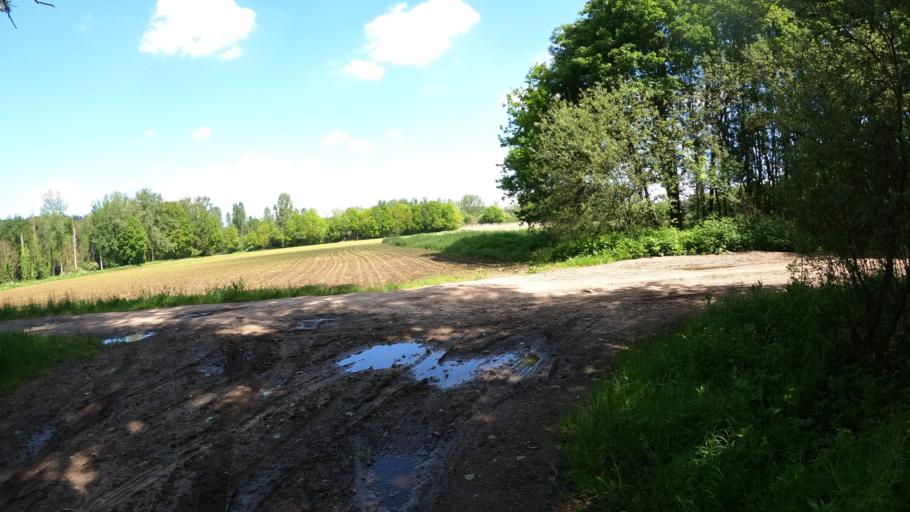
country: BE
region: Flanders
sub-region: Provincie Vlaams-Brabant
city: Boortmeerbeek
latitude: 50.9843
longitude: 4.5884
